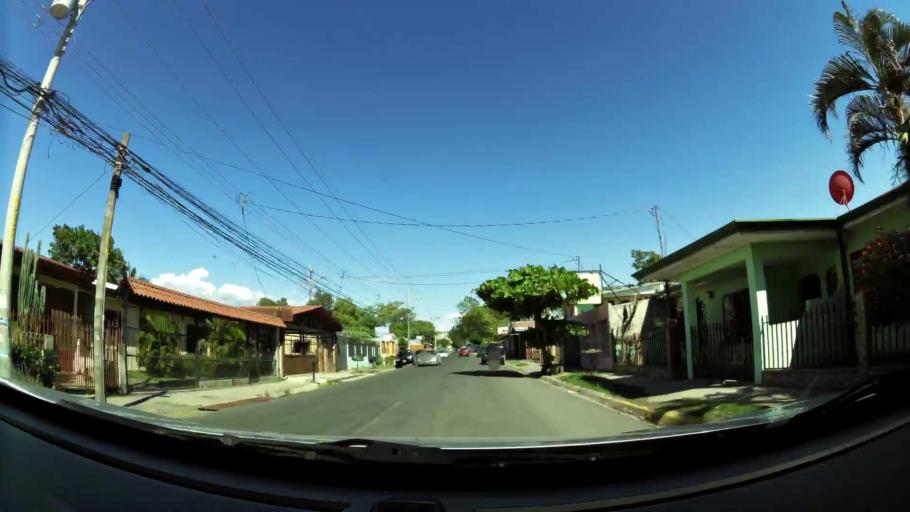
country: CR
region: Guanacaste
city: Liberia
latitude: 10.6317
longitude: -85.4452
